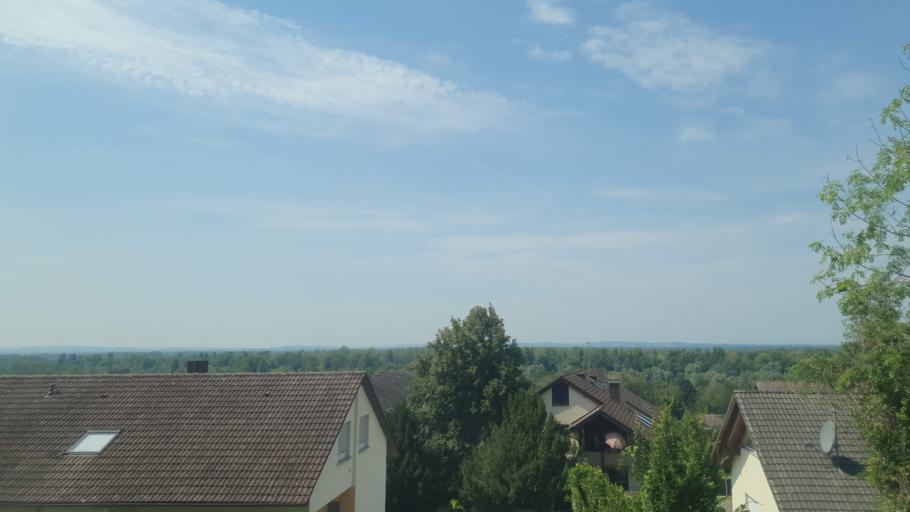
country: DE
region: Baden-Wuerttemberg
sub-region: Freiburg Region
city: Bad Bellingen
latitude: 47.7346
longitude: 7.5565
